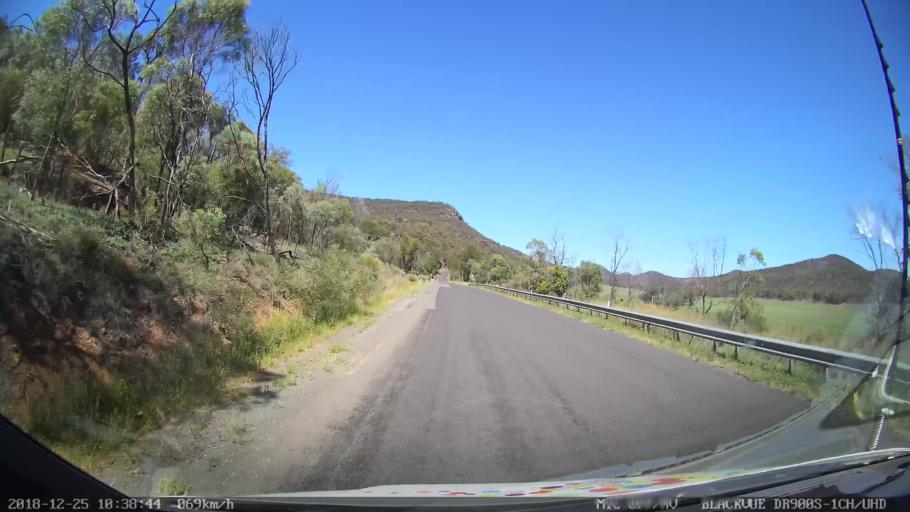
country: AU
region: New South Wales
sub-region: Upper Hunter Shire
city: Merriwa
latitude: -32.4026
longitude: 150.3648
